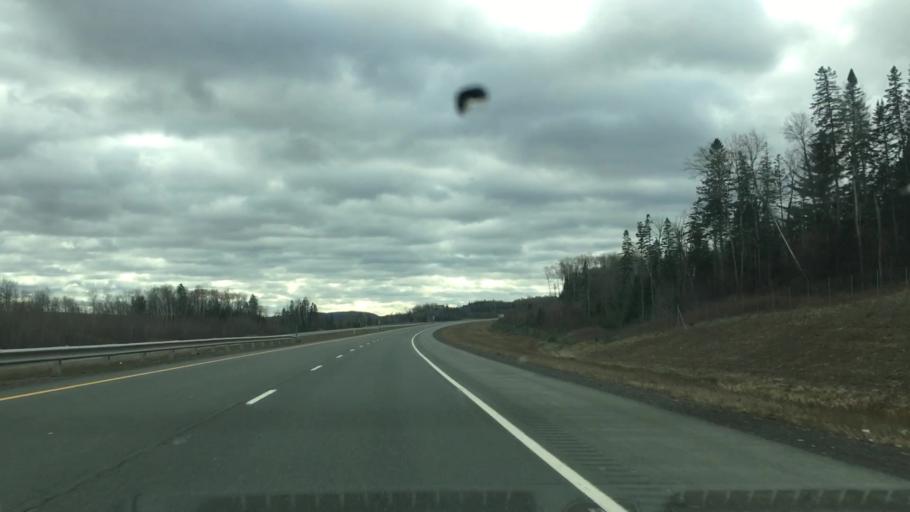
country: US
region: Maine
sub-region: Aroostook County
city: Fort Fairfield
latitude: 46.6759
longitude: -67.7299
